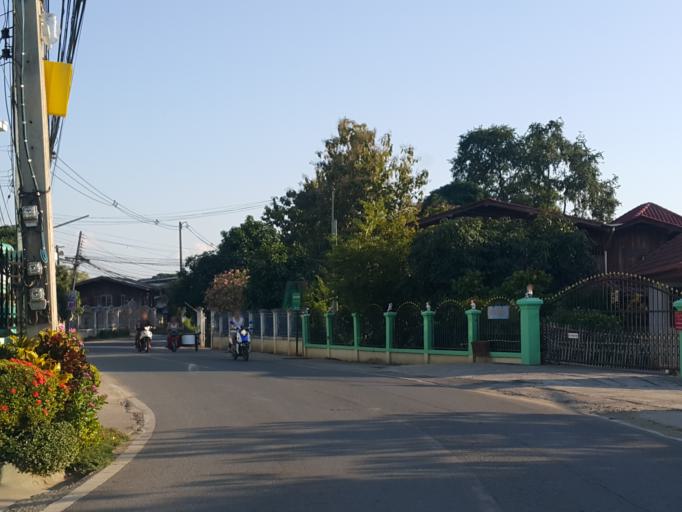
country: TH
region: Chiang Mai
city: San Sai
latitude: 18.7919
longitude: 99.0461
